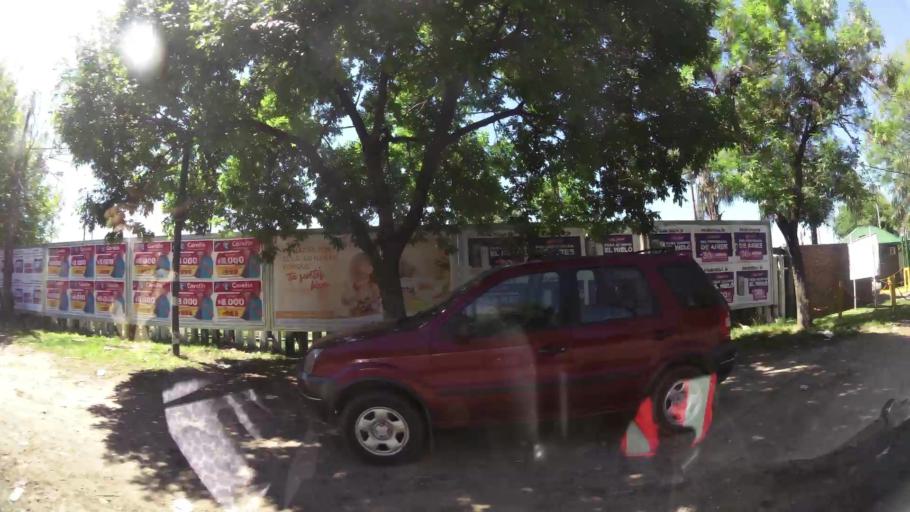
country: AR
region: Santa Fe
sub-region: Departamento de Rosario
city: Rosario
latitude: -32.9336
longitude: -60.6803
